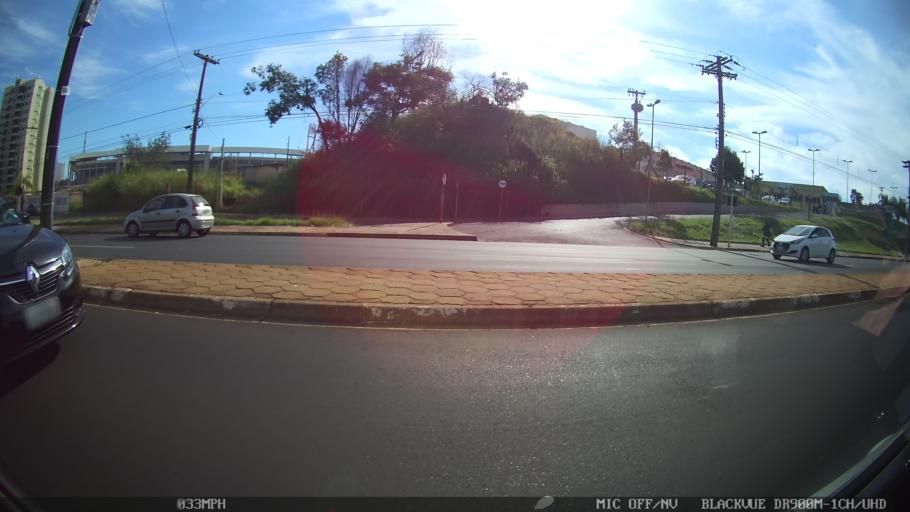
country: BR
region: Sao Paulo
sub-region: Araraquara
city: Araraquara
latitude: -21.7746
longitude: -48.1668
